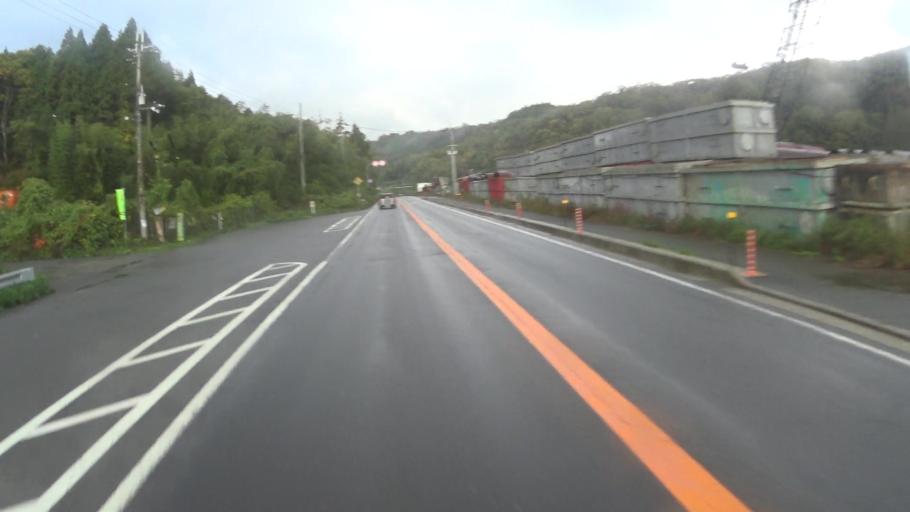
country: JP
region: Kyoto
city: Ayabe
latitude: 35.1817
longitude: 135.3456
